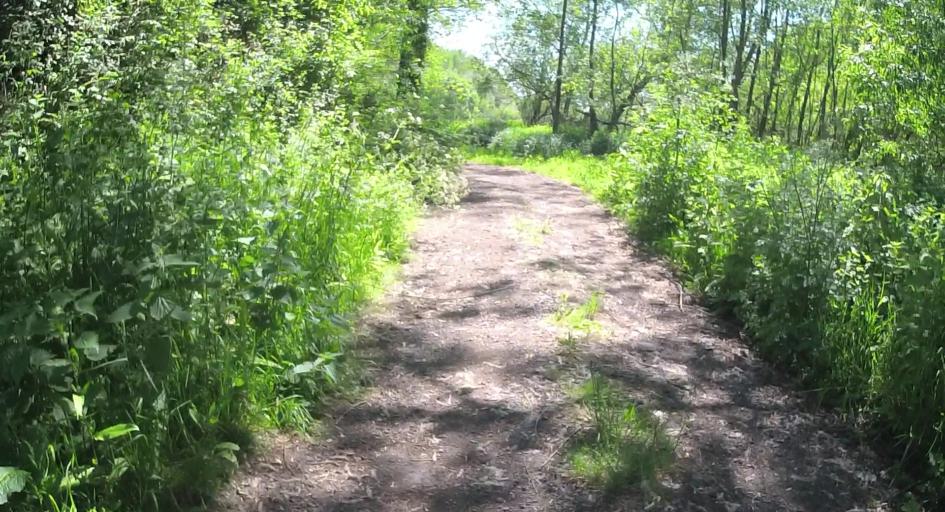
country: GB
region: England
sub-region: West Berkshire
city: Stratfield Mortimer
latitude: 51.3401
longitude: -1.0085
